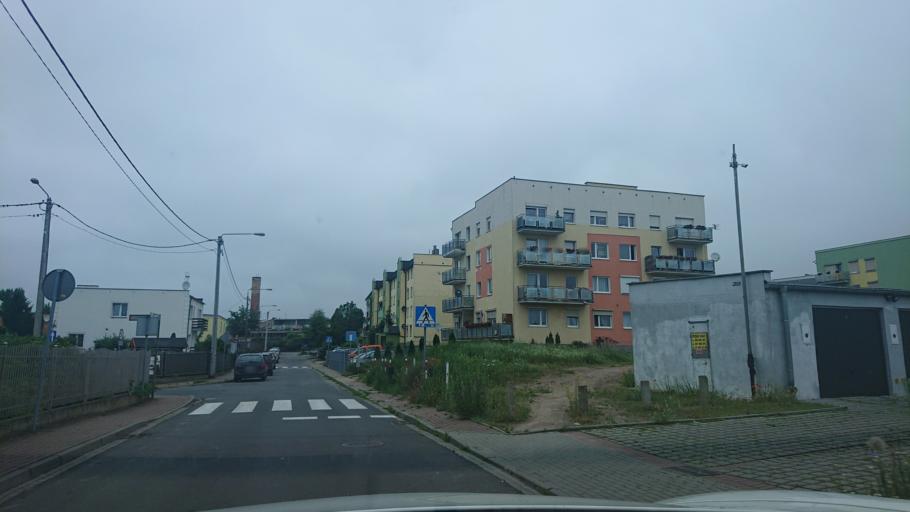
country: PL
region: Greater Poland Voivodeship
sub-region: Powiat gnieznienski
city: Gniezno
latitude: 52.5137
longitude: 17.6004
